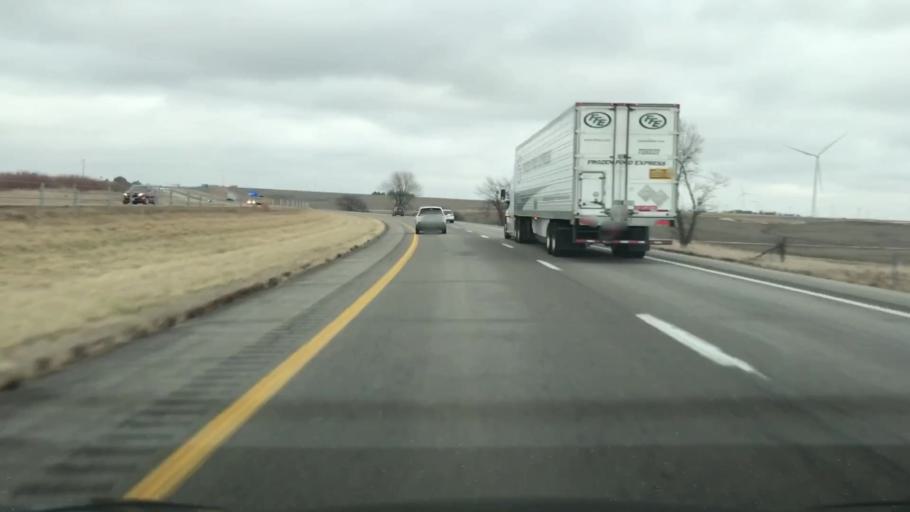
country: US
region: Iowa
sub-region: Guthrie County
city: Stuart
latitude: 41.4935
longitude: -94.3616
